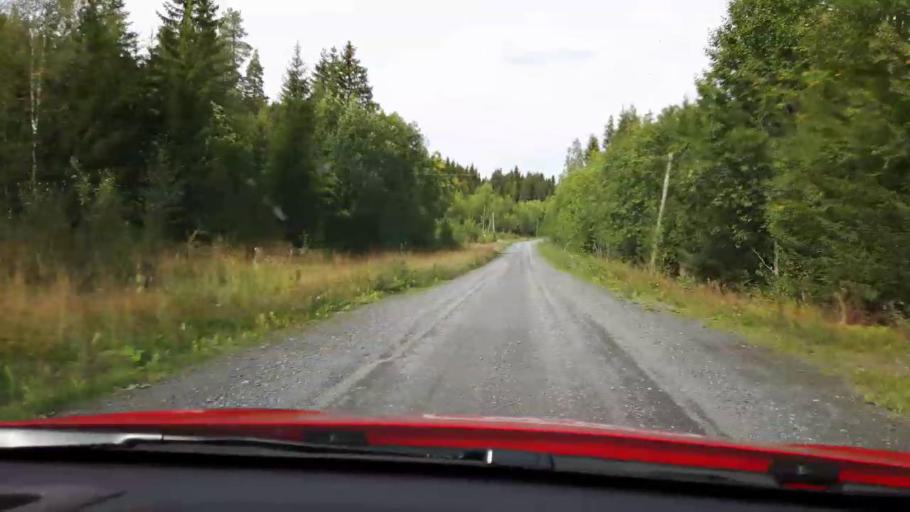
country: SE
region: Jaemtland
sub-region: Are Kommun
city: Jarpen
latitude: 63.2753
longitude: 13.7392
